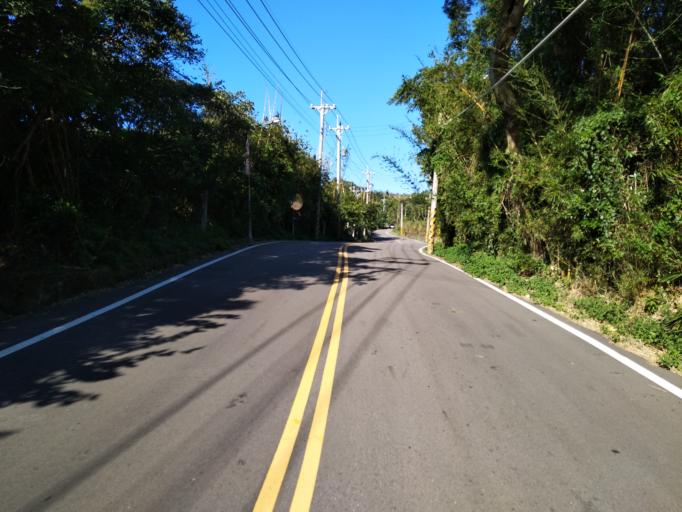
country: TW
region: Taiwan
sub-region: Hsinchu
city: Zhubei
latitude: 24.8653
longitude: 121.0959
